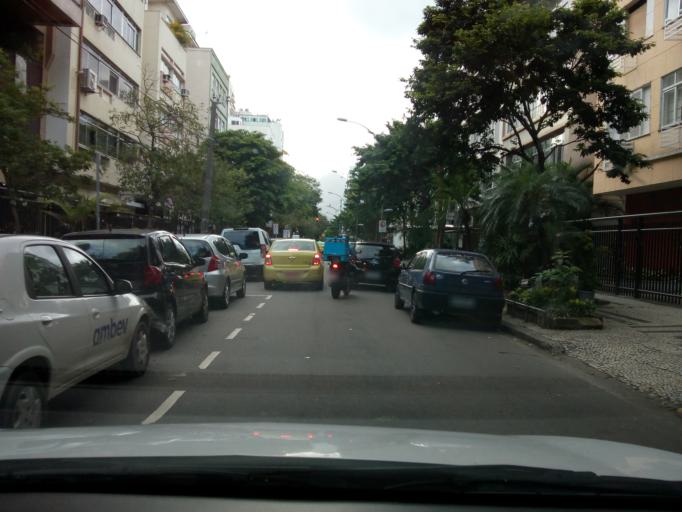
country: BR
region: Rio de Janeiro
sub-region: Rio De Janeiro
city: Rio de Janeiro
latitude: -22.9831
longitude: -43.2016
